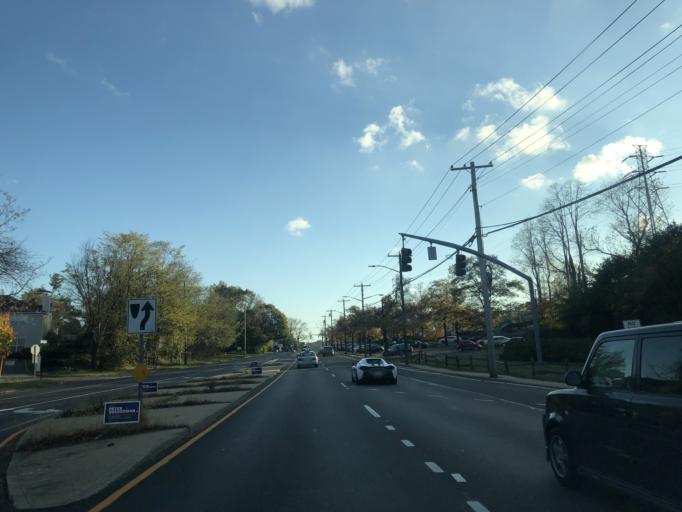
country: US
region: New York
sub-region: Nassau County
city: Greenvale
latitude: 40.8169
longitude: -73.6259
